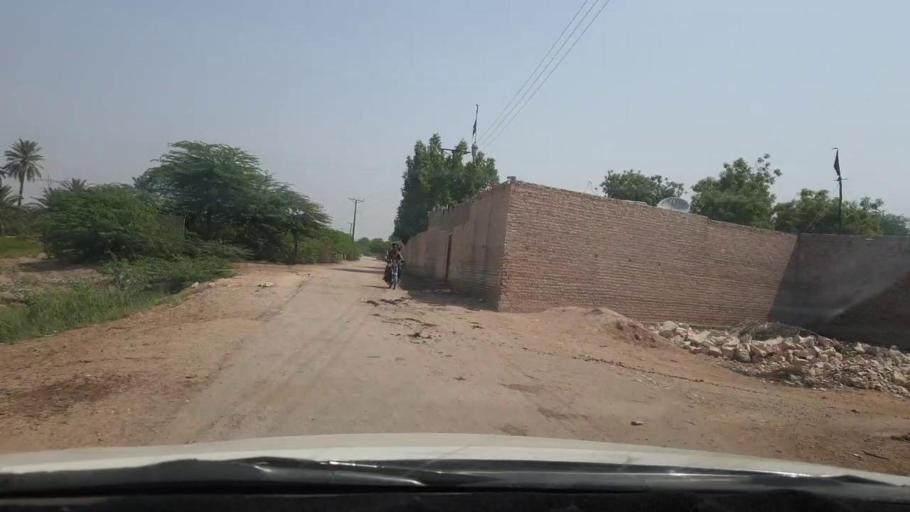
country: PK
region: Sindh
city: Rohri
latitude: 27.6004
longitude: 68.9066
